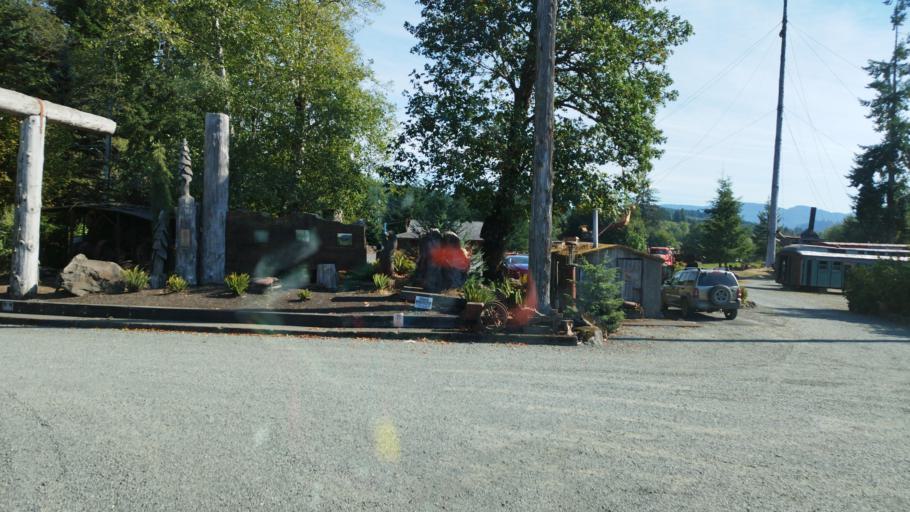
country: US
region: Oregon
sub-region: Clatsop County
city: Seaside
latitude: 45.8864
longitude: -123.6147
